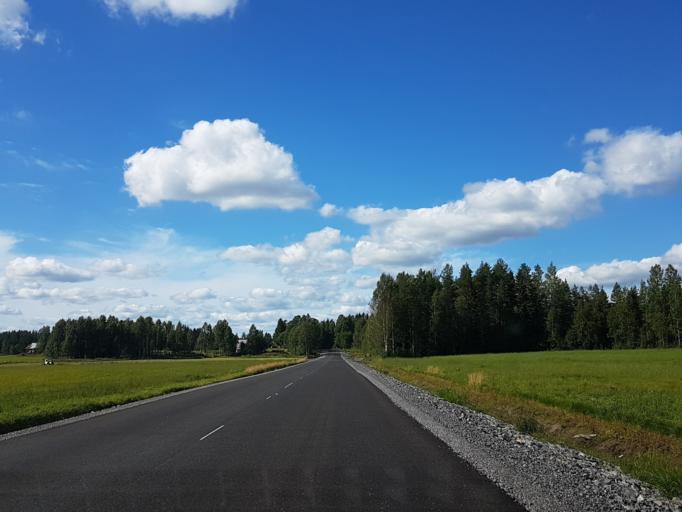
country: SE
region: Vaesterbotten
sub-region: Robertsfors Kommun
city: Robertsfors
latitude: 64.1357
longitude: 20.6308
